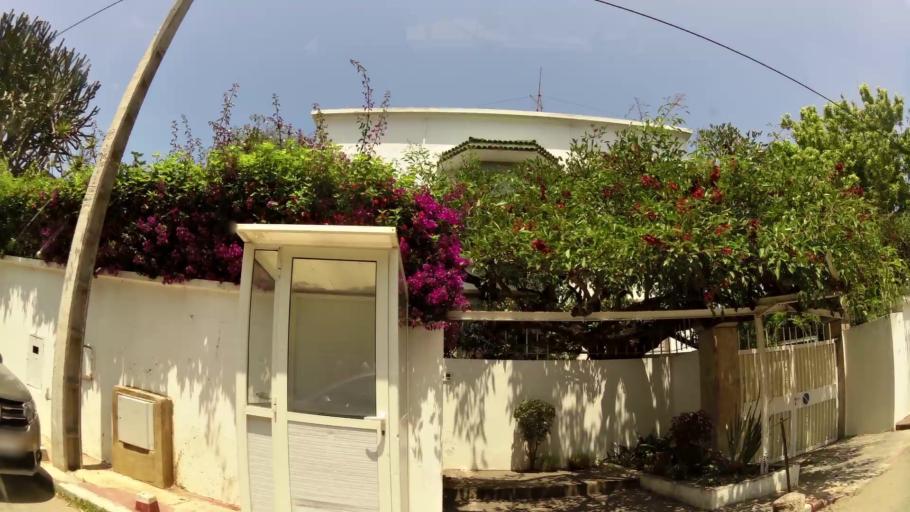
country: MA
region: Rabat-Sale-Zemmour-Zaer
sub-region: Rabat
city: Rabat
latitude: 34.0149
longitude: -6.8224
